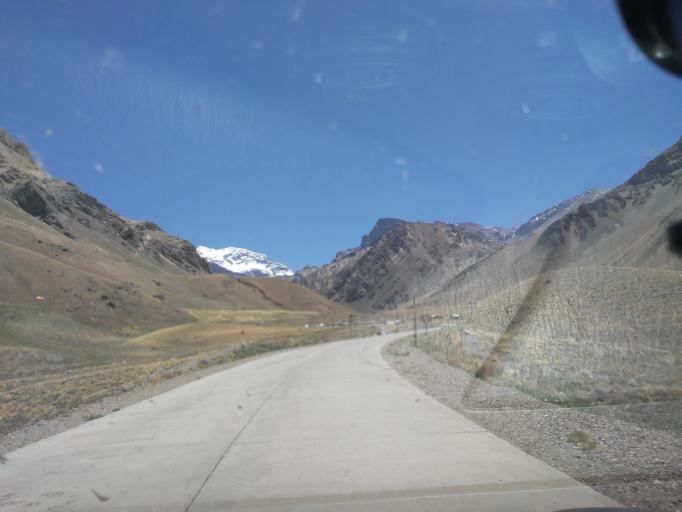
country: CL
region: Valparaiso
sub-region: Provincia de Los Andes
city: Los Andes
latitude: -32.8150
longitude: -69.9422
